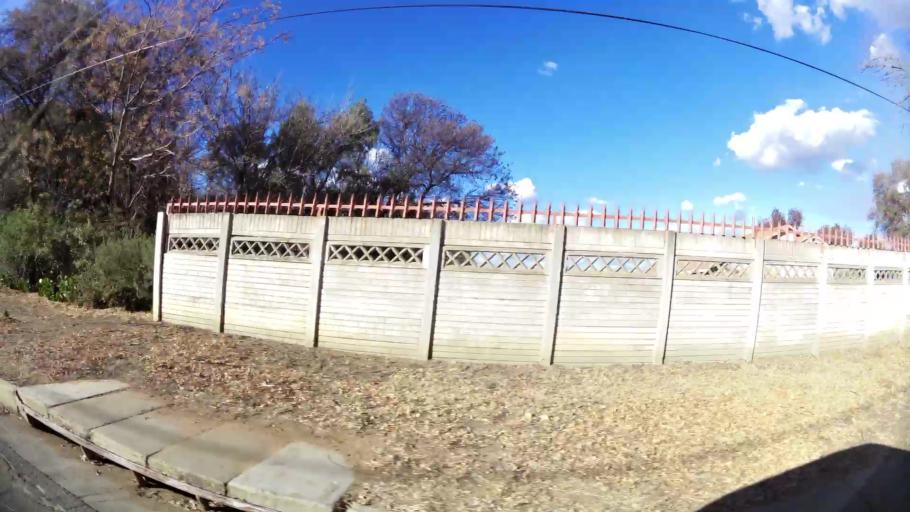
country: ZA
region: North-West
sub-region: Dr Kenneth Kaunda District Municipality
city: Klerksdorp
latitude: -26.8399
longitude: 26.6626
